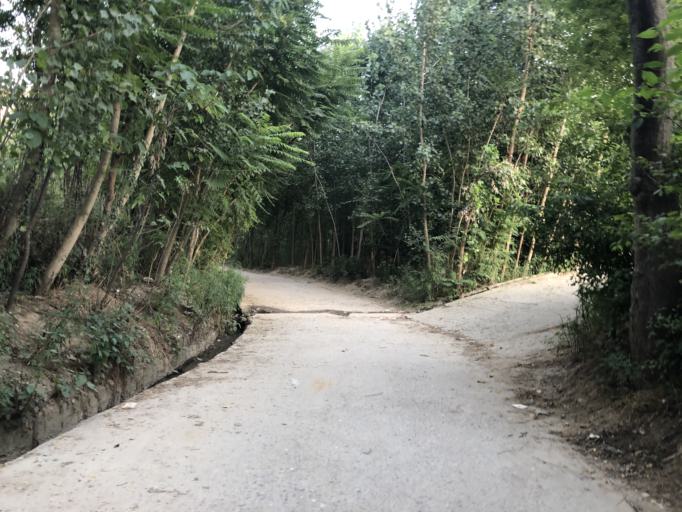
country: PK
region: Khyber Pakhtunkhwa
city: Daggar
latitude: 34.5799
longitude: 72.4547
